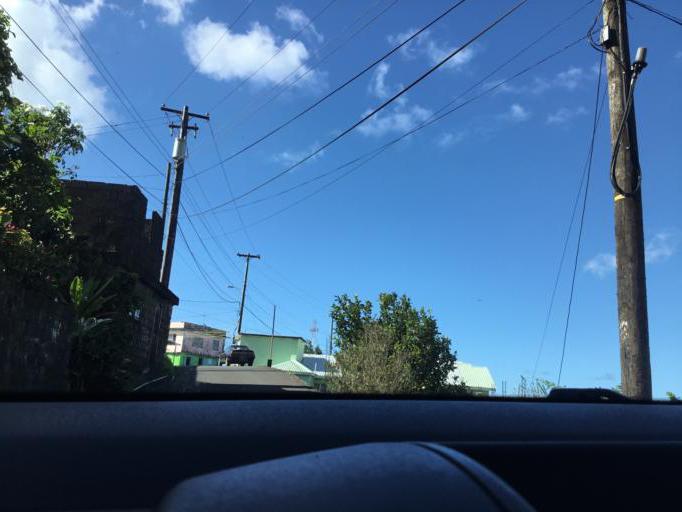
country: VC
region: Saint David
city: Chateaubelair
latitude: 13.2706
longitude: -61.2408
